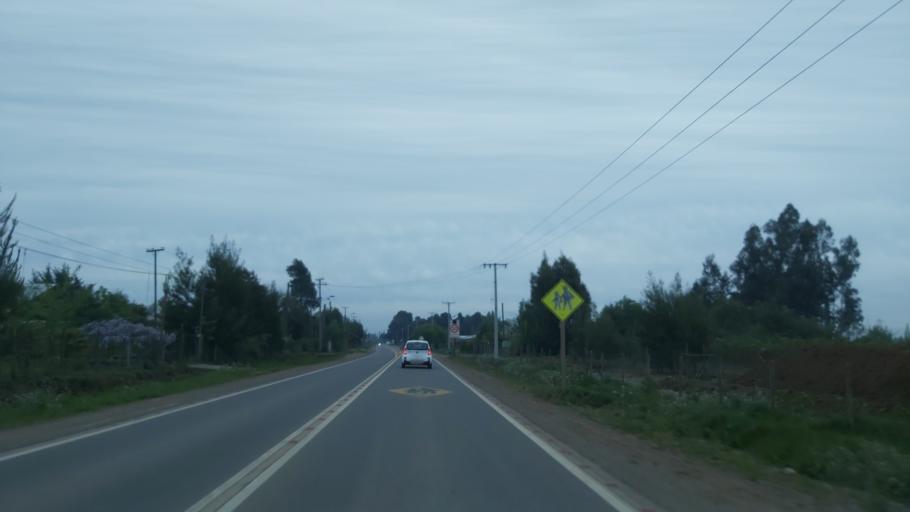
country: CL
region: Maule
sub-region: Provincia de Linares
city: Colbun
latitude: -35.7164
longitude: -71.4827
